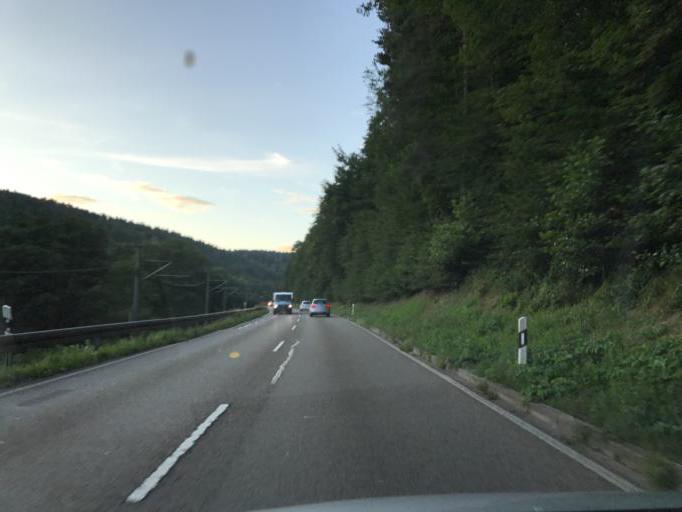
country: DE
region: Baden-Wuerttemberg
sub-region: Karlsruhe Region
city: Ettlingen
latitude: 48.8906
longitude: 8.4512
